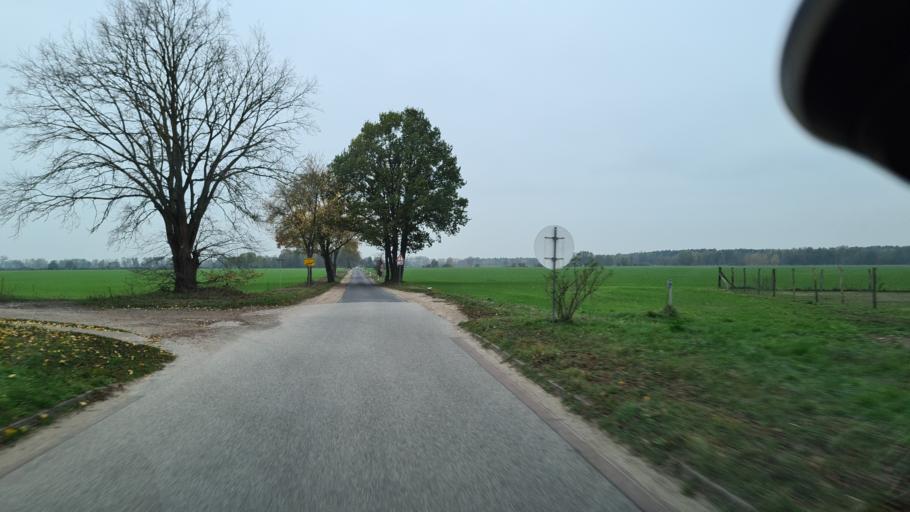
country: DE
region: Brandenburg
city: Lindow
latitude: 52.9321
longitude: 13.0128
